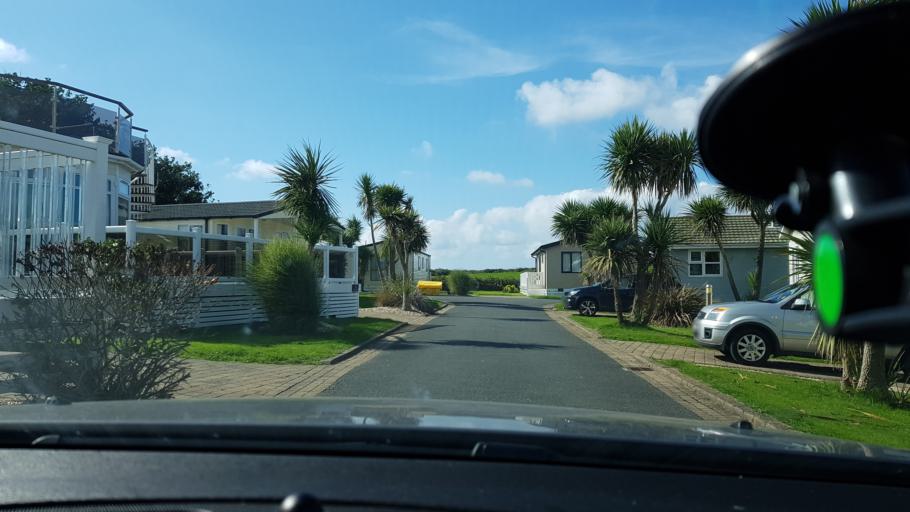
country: GB
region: England
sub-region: Cornwall
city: Tintagel
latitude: 50.6691
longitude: -4.7421
